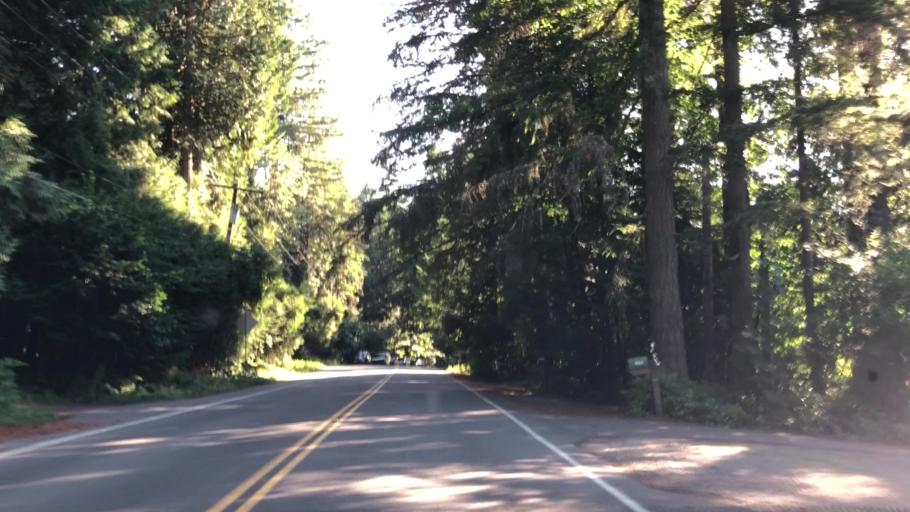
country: US
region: Washington
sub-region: King County
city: Cottage Lake
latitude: 47.7587
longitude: -122.1187
